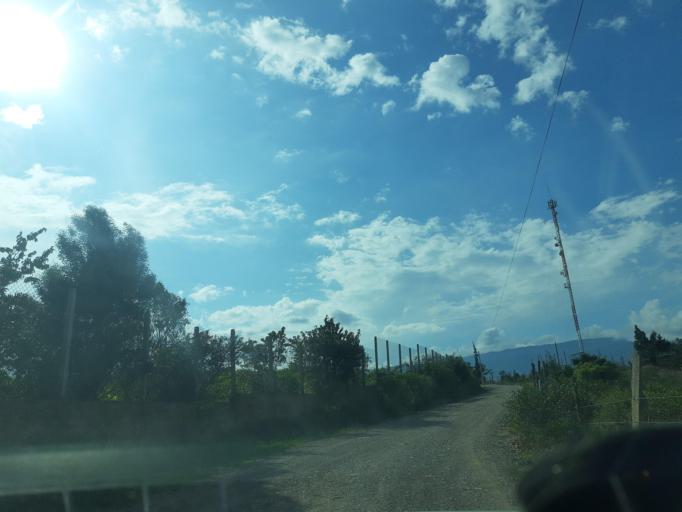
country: CO
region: Boyaca
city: Villa de Leiva
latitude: 5.6596
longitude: -73.5467
